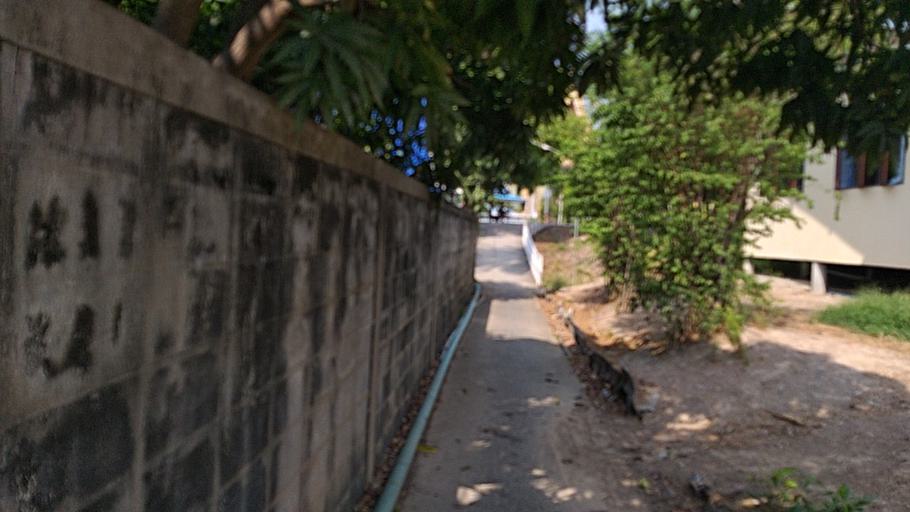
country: TH
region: Pathum Thani
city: Sam Khok
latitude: 14.1147
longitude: 100.5355
